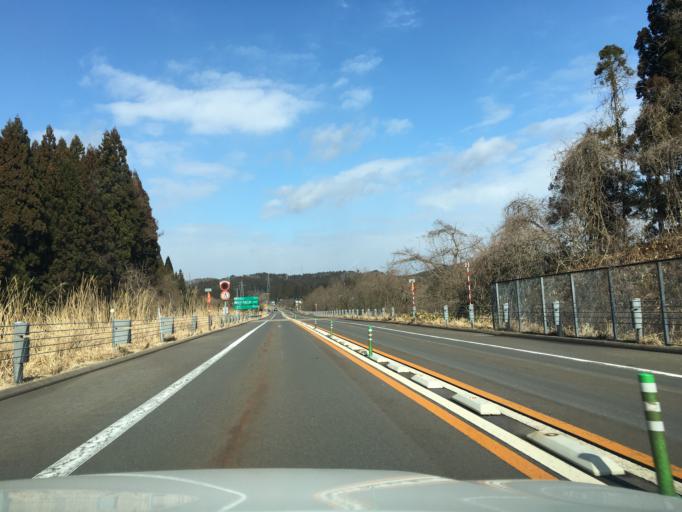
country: JP
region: Akita
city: Akita
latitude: 39.7335
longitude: 140.1765
